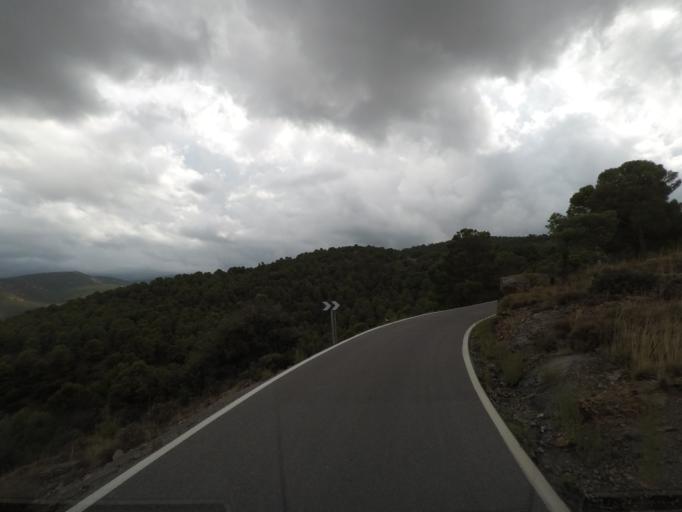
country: ES
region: Andalusia
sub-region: Provincia de Granada
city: Ferreira
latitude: 37.1691
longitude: -3.0480
